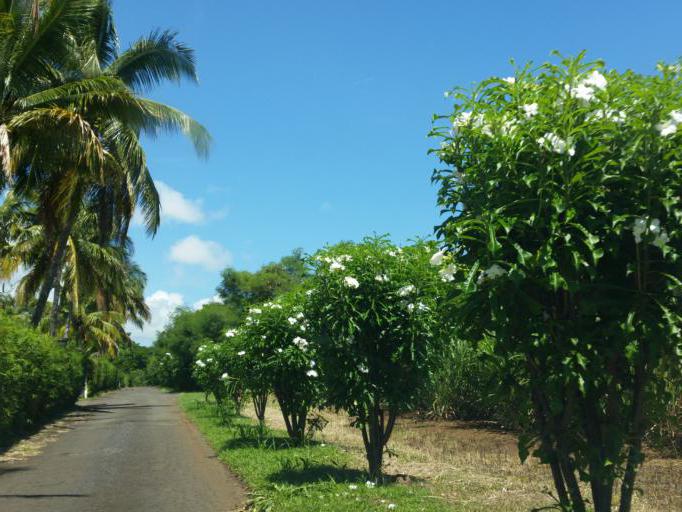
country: RE
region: Reunion
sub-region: Reunion
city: Sainte-Marie
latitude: -20.9061
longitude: 55.5175
